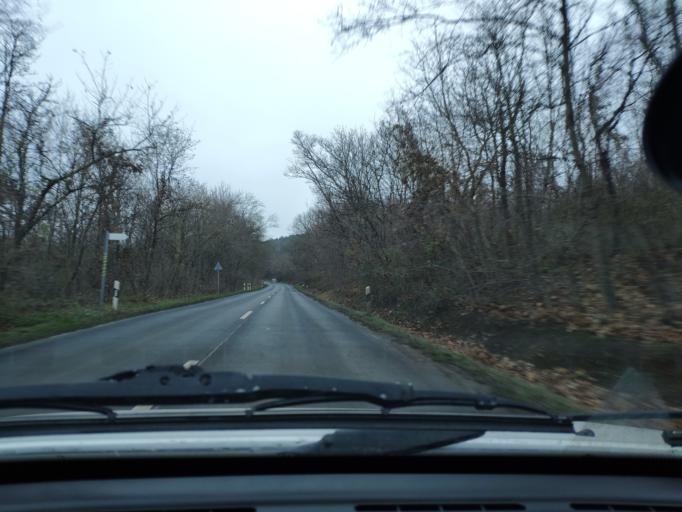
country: HU
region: Pest
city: Soskut
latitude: 47.4346
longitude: 18.8227
